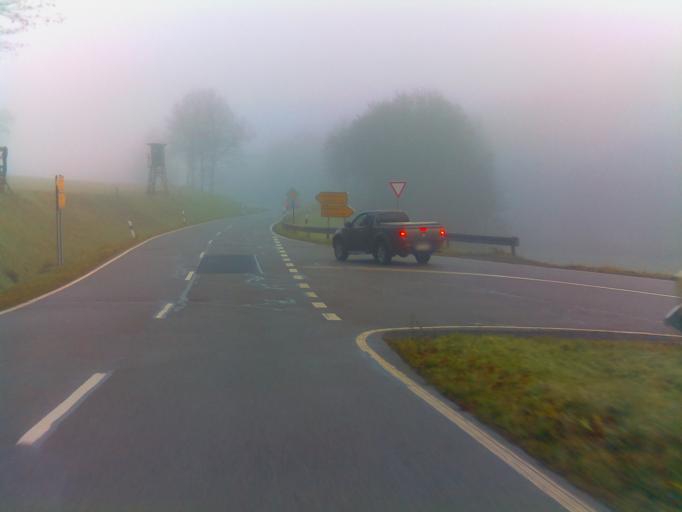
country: DE
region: Bavaria
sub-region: Regierungsbezirk Unterfranken
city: Neunkirchen
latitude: 49.6659
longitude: 9.3699
